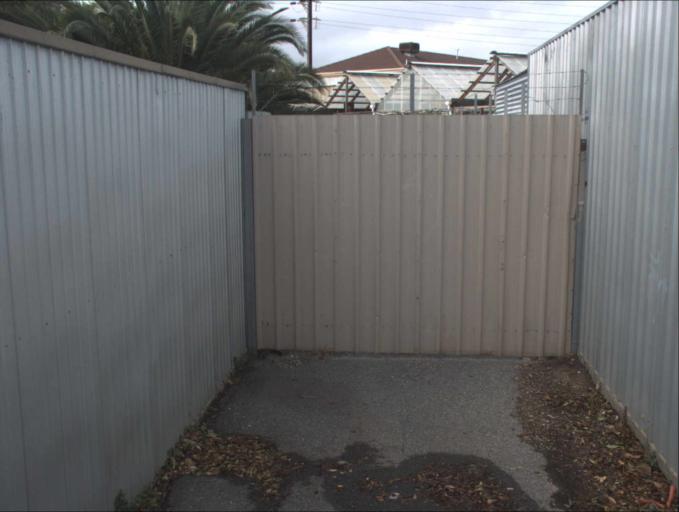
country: AU
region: South Australia
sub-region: Port Adelaide Enfield
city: Birkenhead
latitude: -34.8390
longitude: 138.4883
